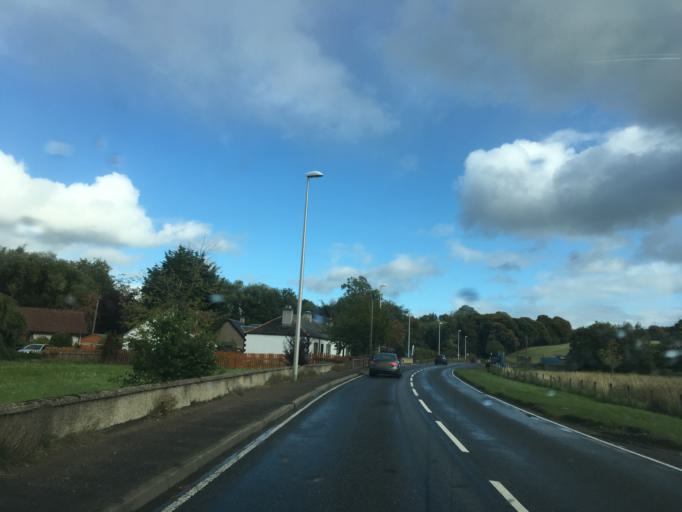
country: GB
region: Scotland
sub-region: Highland
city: Beauly
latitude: 57.4725
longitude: -4.3865
